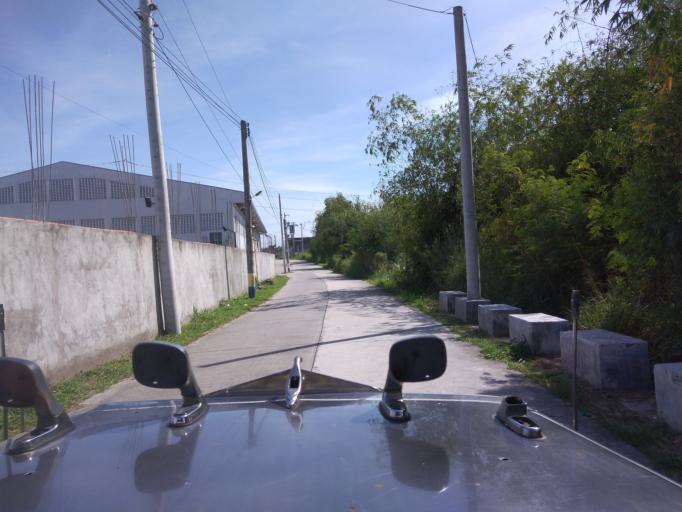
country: PH
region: Central Luzon
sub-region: Province of Pampanga
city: San Juan
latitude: 15.0222
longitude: 120.6677
